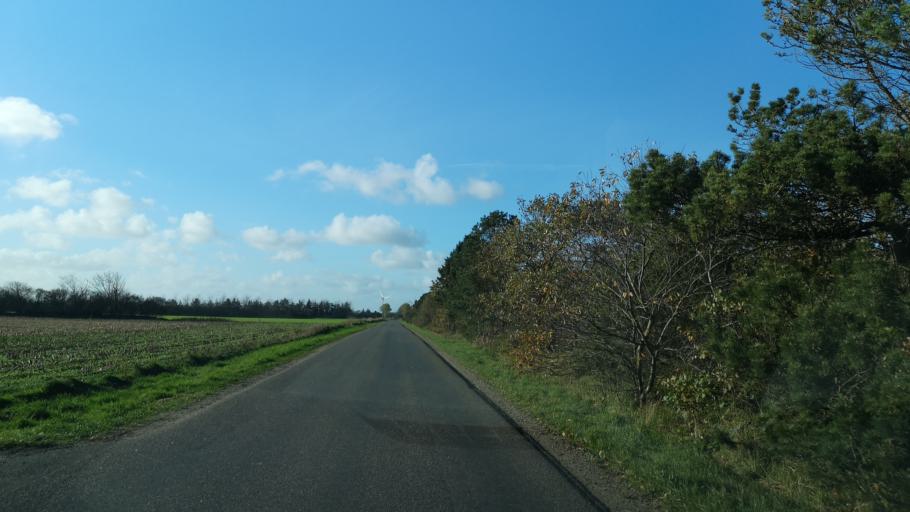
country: DK
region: Central Jutland
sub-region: Ringkobing-Skjern Kommune
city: Skjern
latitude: 55.8325
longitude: 8.3753
